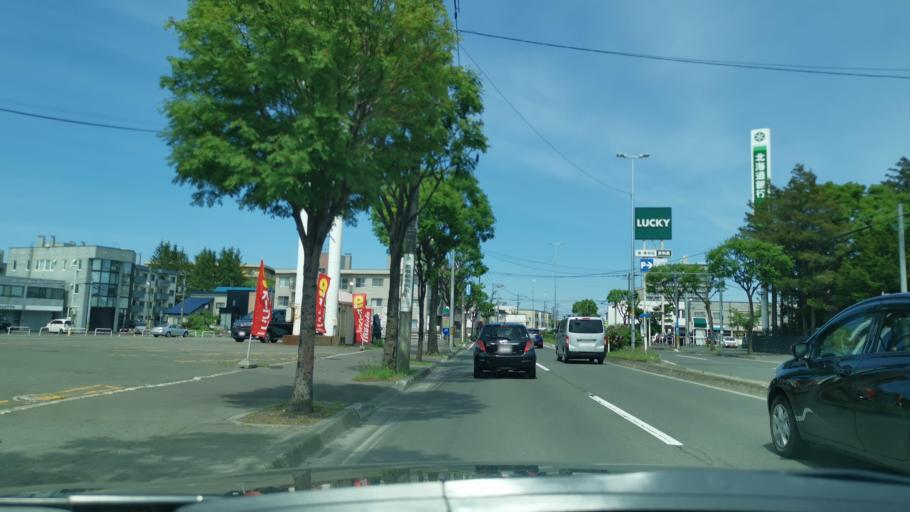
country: JP
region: Hokkaido
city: Sapporo
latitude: 43.0685
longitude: 141.4019
